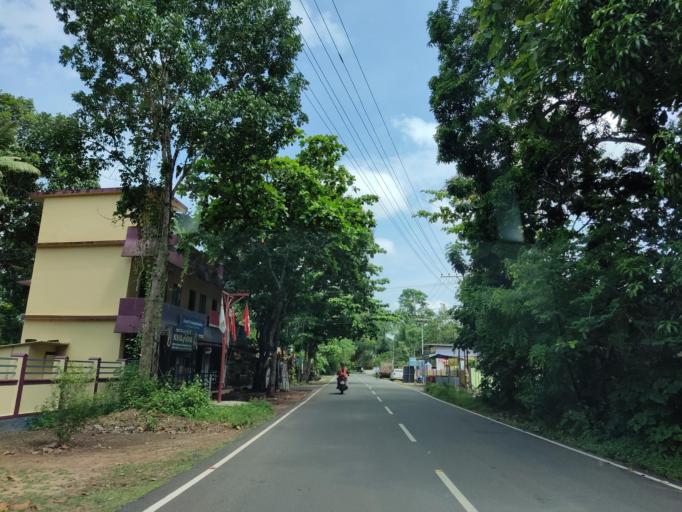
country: IN
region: Kerala
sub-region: Alappuzha
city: Mavelikara
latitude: 9.2703
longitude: 76.5670
